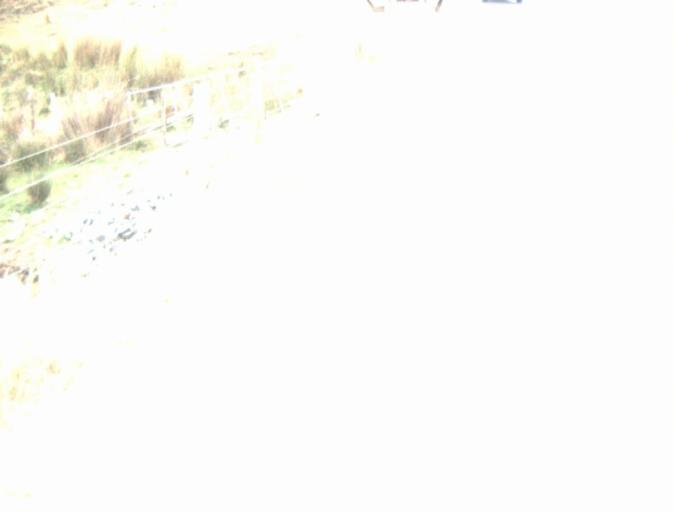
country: AU
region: Tasmania
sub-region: Dorset
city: Scottsdale
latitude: -41.4724
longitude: 147.5874
